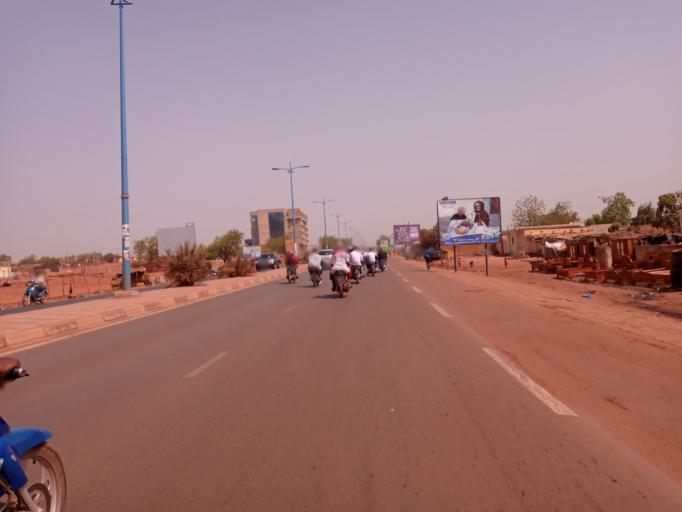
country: ML
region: Bamako
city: Bamako
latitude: 12.5966
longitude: -7.9926
